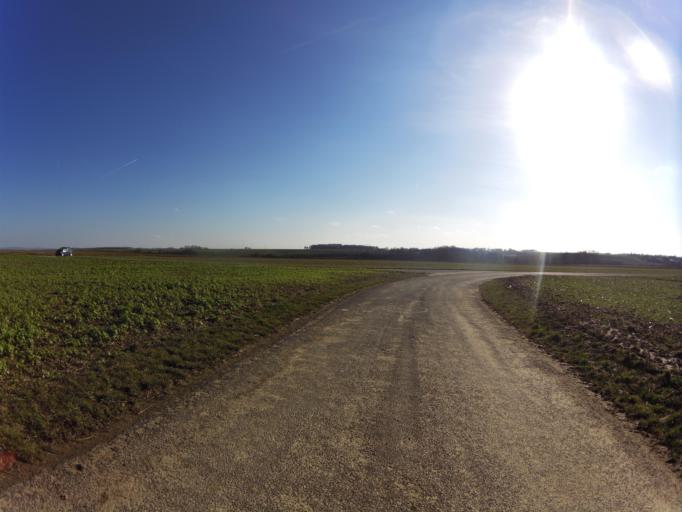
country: DE
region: Bavaria
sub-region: Regierungsbezirk Unterfranken
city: Giebelstadt
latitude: 49.6756
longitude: 9.9744
